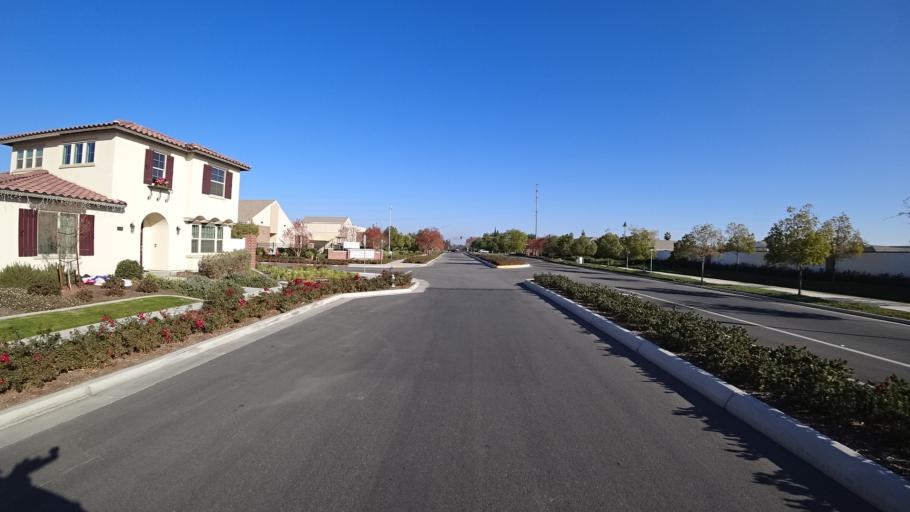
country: US
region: California
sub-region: Kern County
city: Rosedale
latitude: 35.3178
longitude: -119.1300
